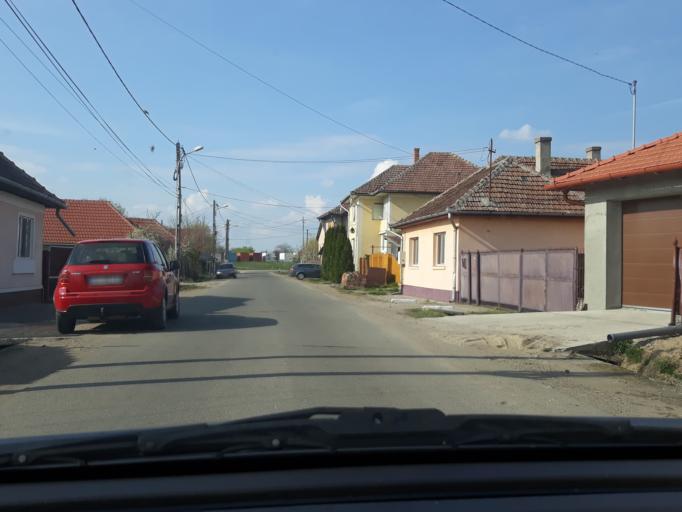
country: RO
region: Bihor
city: Margita
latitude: 47.3485
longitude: 22.3286
